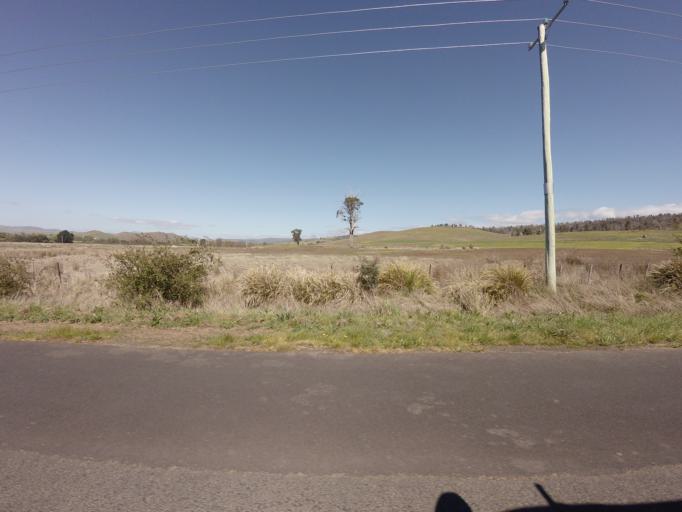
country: AU
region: Tasmania
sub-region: Derwent Valley
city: New Norfolk
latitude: -42.5370
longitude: 146.7255
